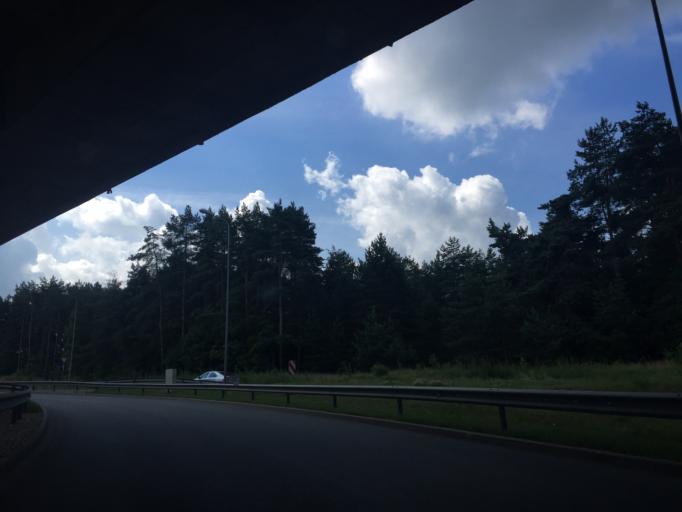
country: LV
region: Kekava
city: Balozi
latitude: 56.9013
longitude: 24.1336
